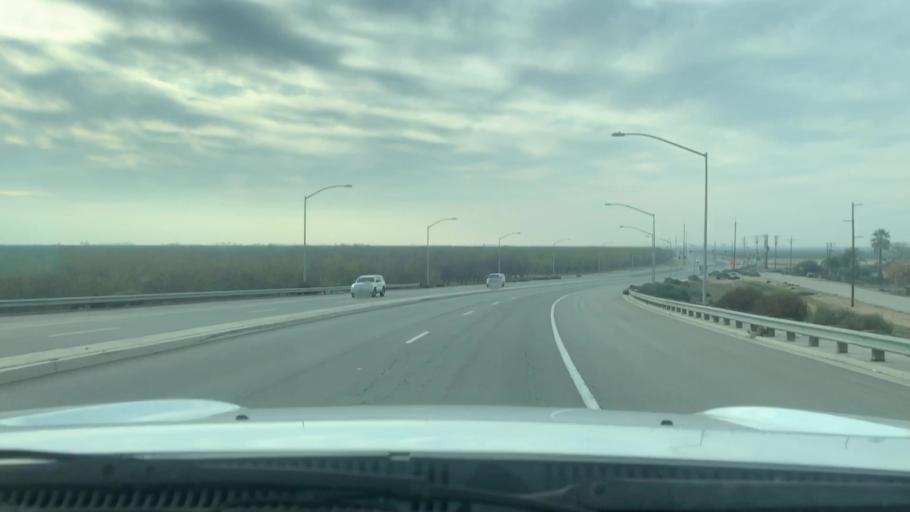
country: US
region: California
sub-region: Kern County
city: Rosedale
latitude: 35.4412
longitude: -119.2006
